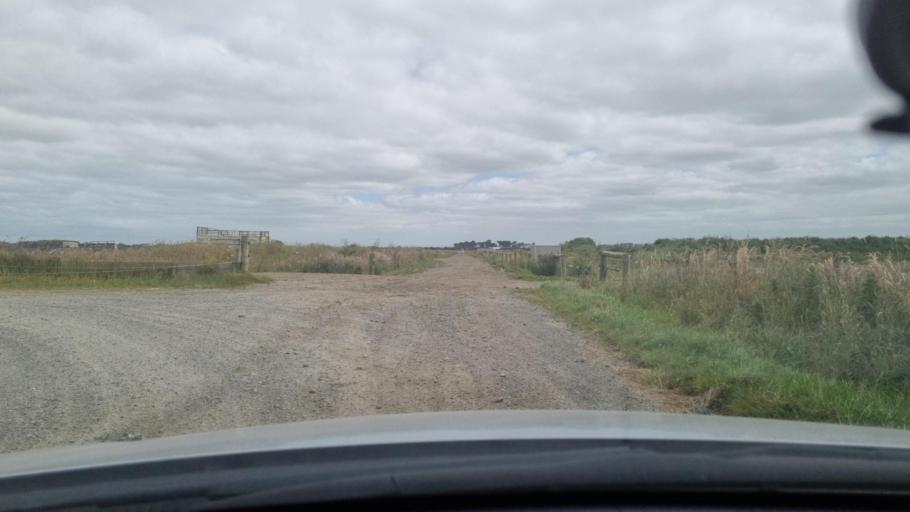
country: NZ
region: Southland
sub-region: Invercargill City
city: Invercargill
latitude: -46.4211
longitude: 168.3107
